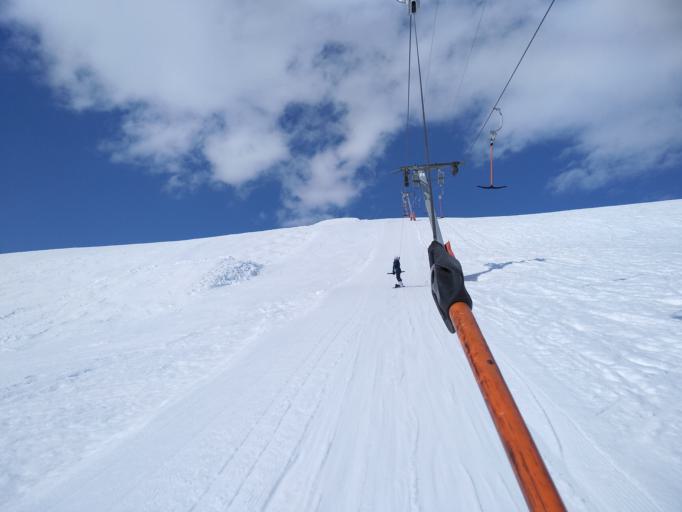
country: NO
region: Sogn og Fjordane
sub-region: Vik
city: Vik
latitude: 60.8658
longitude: 6.4603
